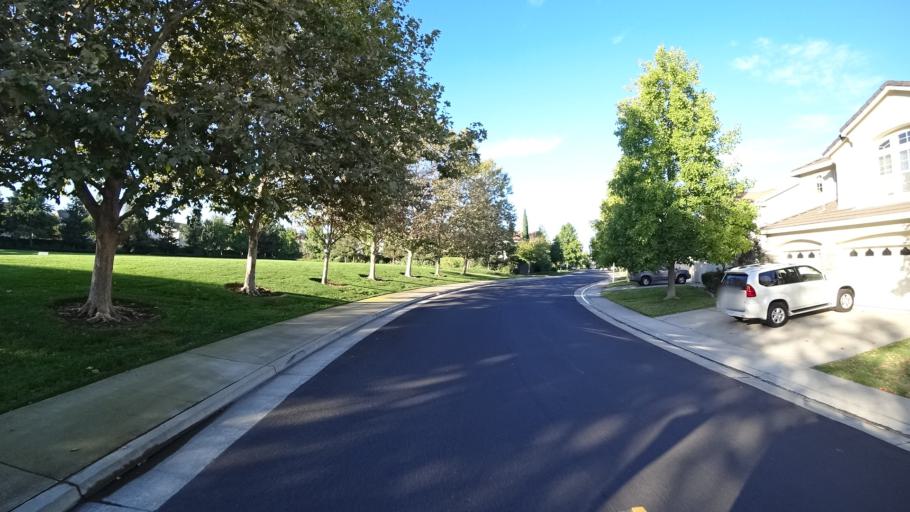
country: US
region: California
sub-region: Sacramento County
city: Laguna
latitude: 38.3977
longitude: -121.4782
